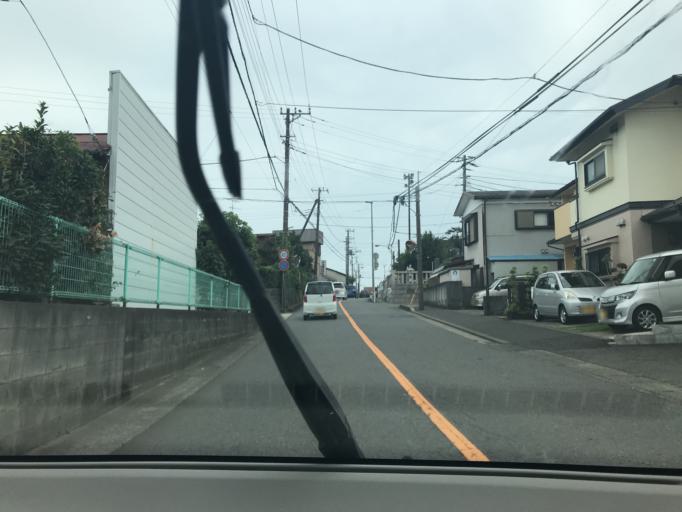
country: JP
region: Kanagawa
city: Fujisawa
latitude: 35.3847
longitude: 139.4389
